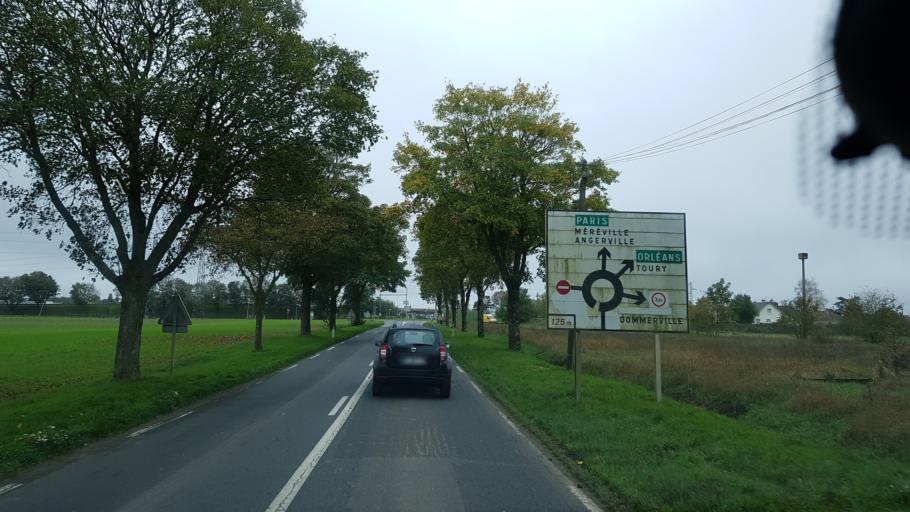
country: FR
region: Ile-de-France
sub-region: Departement de l'Essonne
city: Angerville
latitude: 48.3202
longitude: 1.9958
